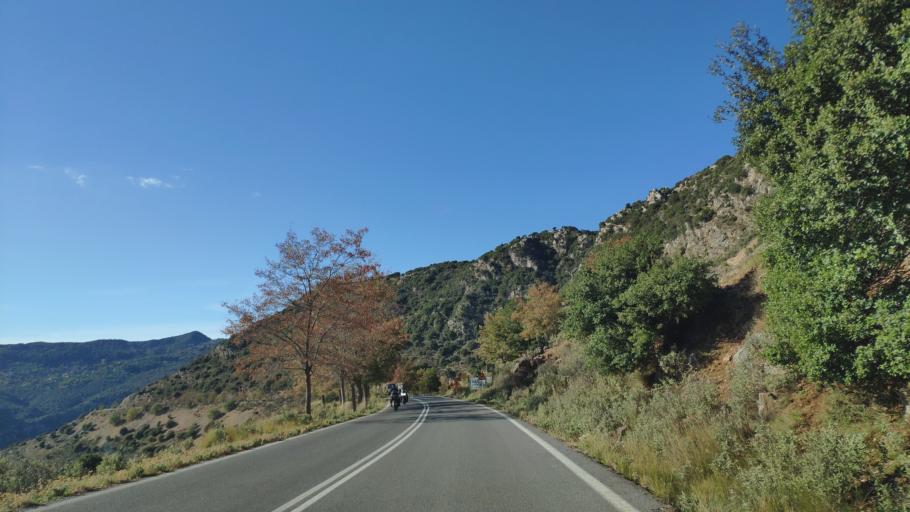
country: GR
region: Peloponnese
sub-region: Nomos Arkadias
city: Dimitsana
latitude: 37.5803
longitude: 22.0576
